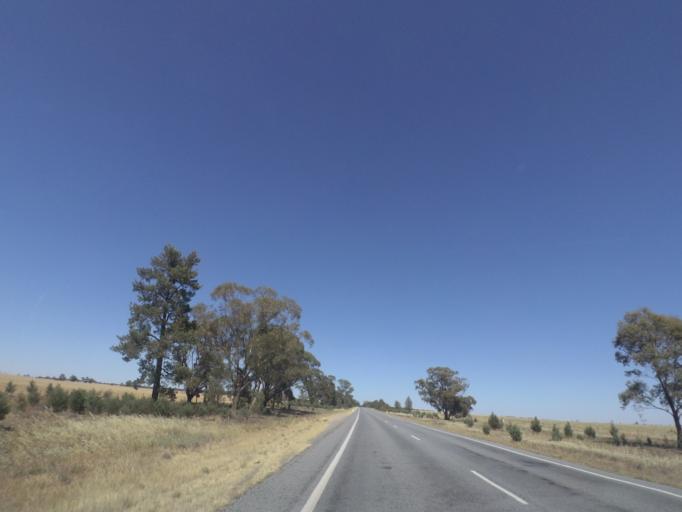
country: AU
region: New South Wales
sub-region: Narrandera
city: Narrandera
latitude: -34.4130
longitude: 146.8698
